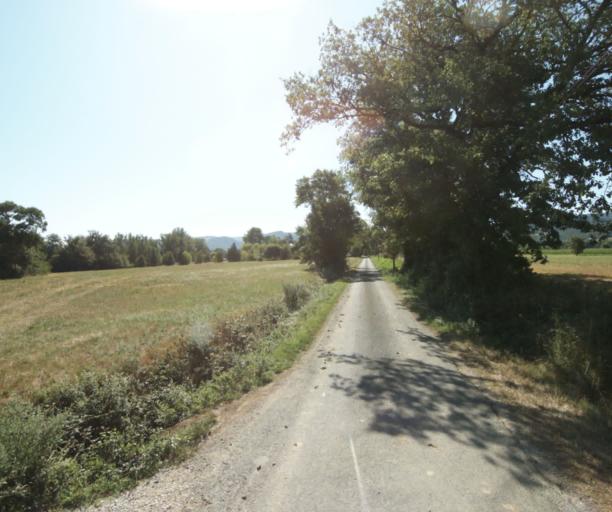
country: FR
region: Midi-Pyrenees
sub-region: Departement de la Haute-Garonne
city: Revel
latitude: 43.4603
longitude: 2.0284
